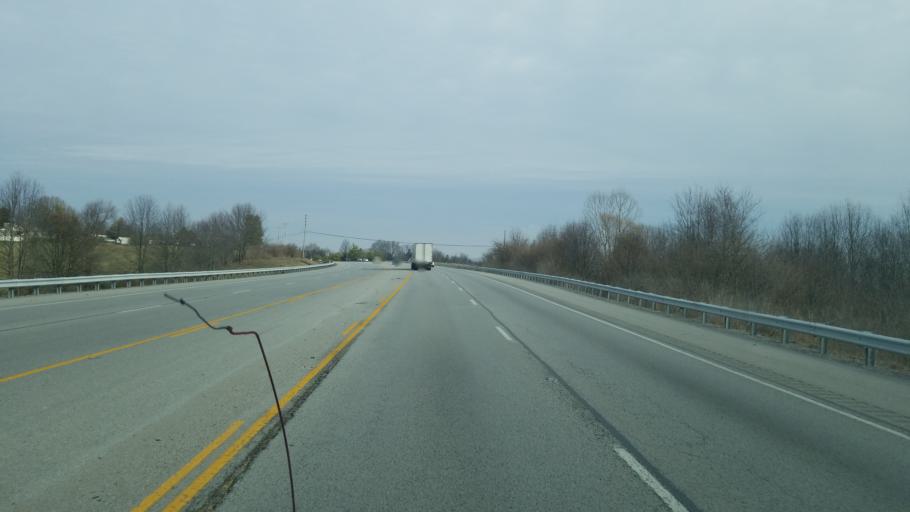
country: US
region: Kentucky
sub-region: Boyle County
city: Junction City
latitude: 37.5964
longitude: -84.7759
